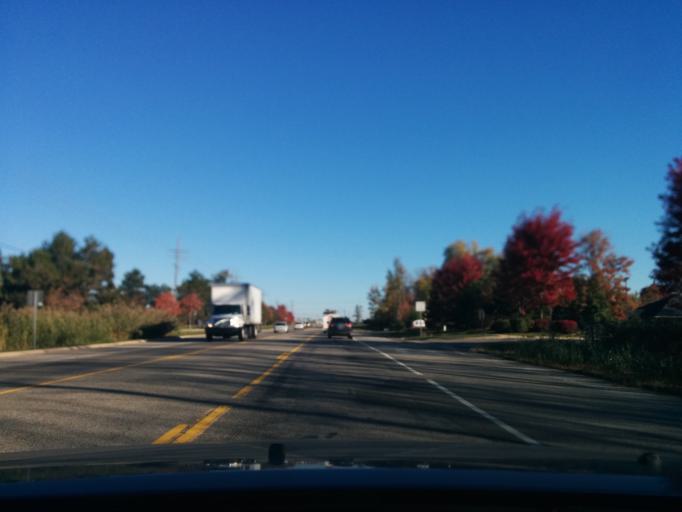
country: US
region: Michigan
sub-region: Oakland County
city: Novi
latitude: 42.4858
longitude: -83.5153
